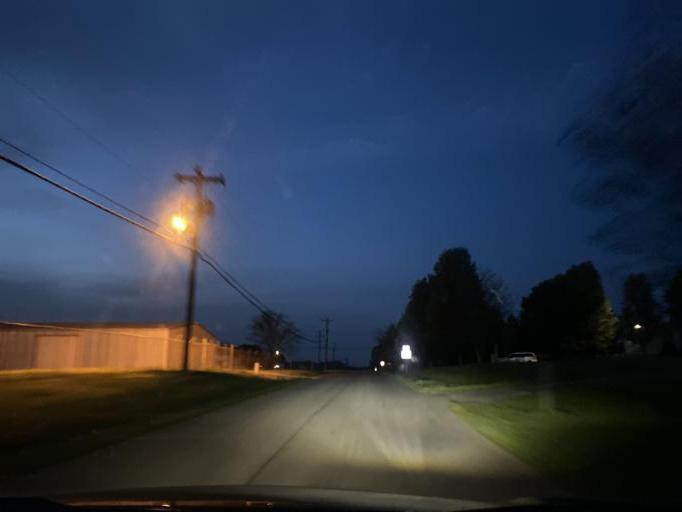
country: US
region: South Carolina
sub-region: Spartanburg County
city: Mayo
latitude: 35.1270
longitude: -81.7878
